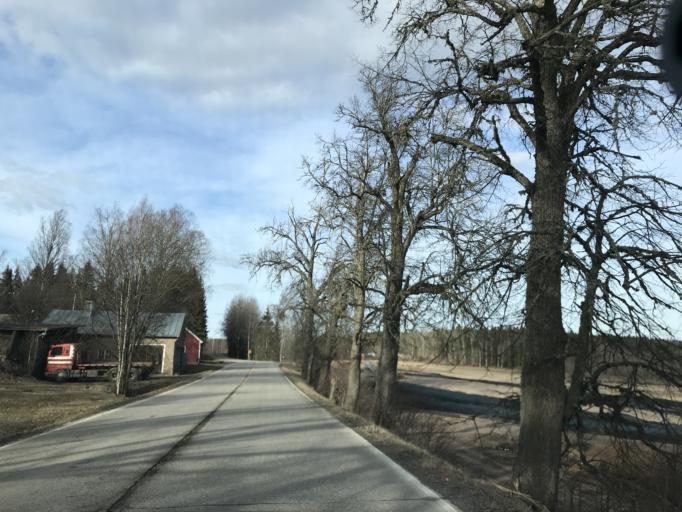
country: FI
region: Uusimaa
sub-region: Raaseporin
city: Ekenaes
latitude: 60.0843
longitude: 23.4110
